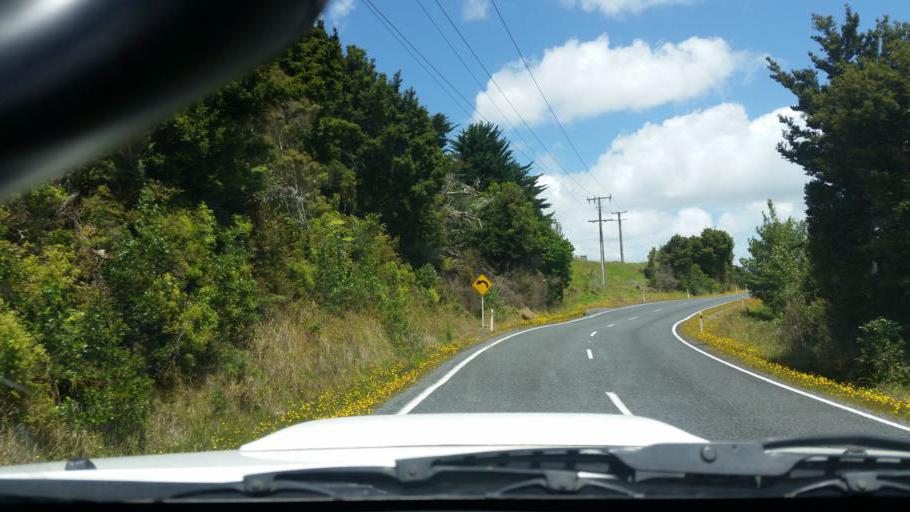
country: NZ
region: Northland
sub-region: Whangarei
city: Ruakaka
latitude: -36.0572
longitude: 174.2729
